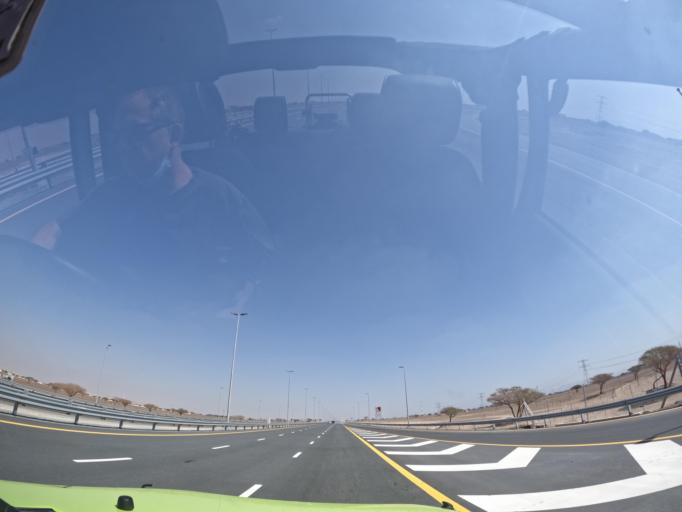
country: AE
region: Ash Shariqah
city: Adh Dhayd
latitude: 24.9574
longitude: 55.8392
